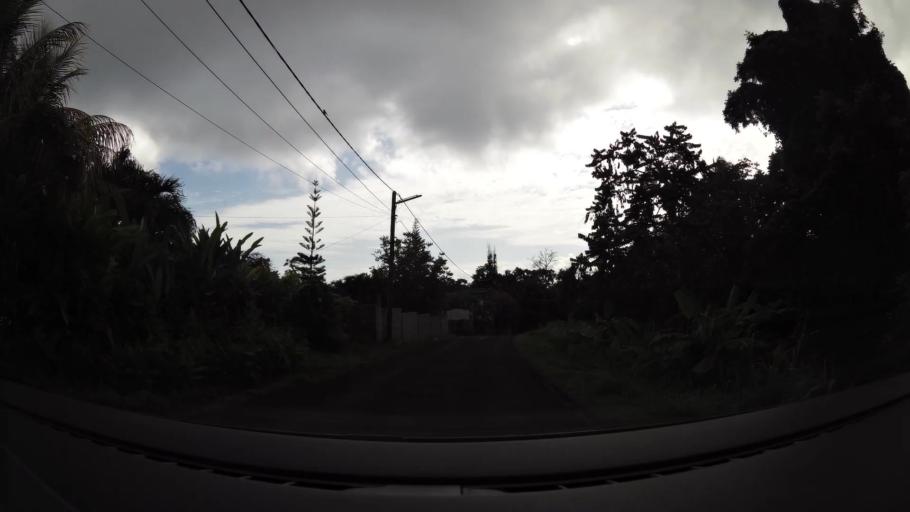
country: GP
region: Guadeloupe
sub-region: Guadeloupe
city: Trois-Rivieres
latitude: 15.9815
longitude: -61.6367
